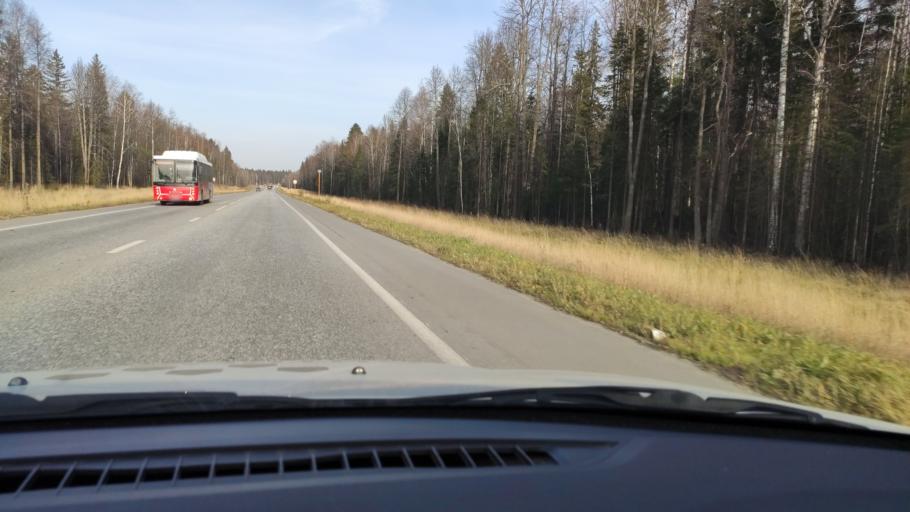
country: RU
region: Perm
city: Novyye Lyady
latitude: 58.0429
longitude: 56.5424
